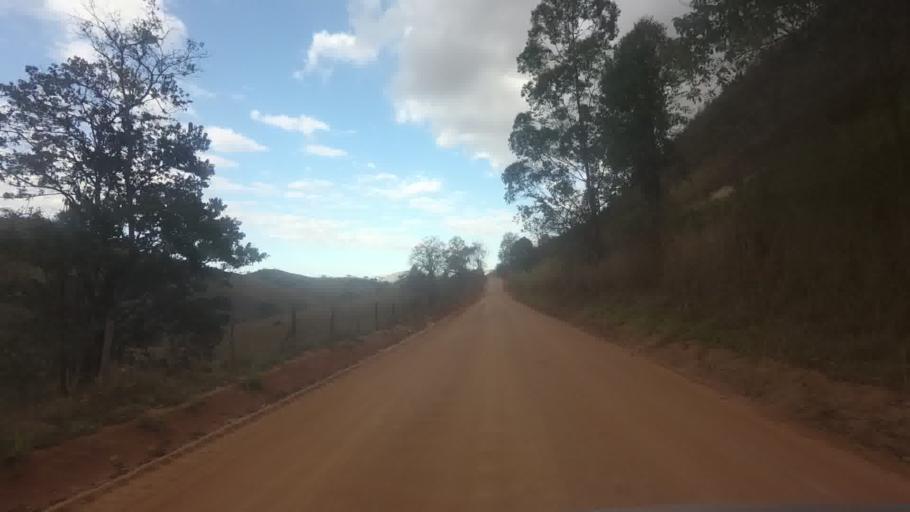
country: BR
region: Espirito Santo
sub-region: Mimoso Do Sul
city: Mimoso do Sul
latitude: -20.9478
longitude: -41.3870
